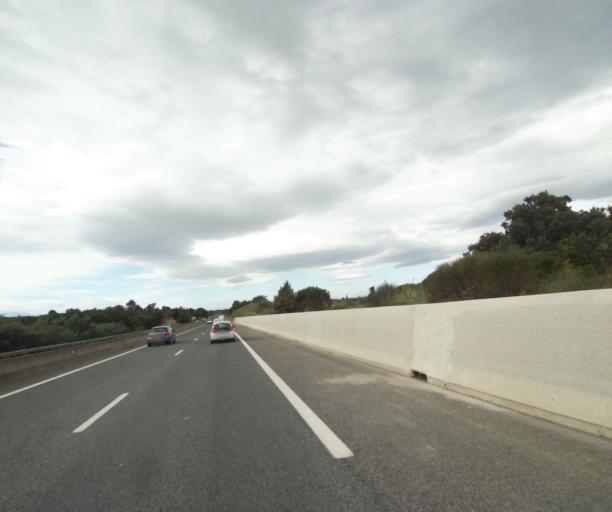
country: FR
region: Languedoc-Roussillon
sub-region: Departement des Pyrenees-Orientales
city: Argelers
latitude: 42.5392
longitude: 3.0236
